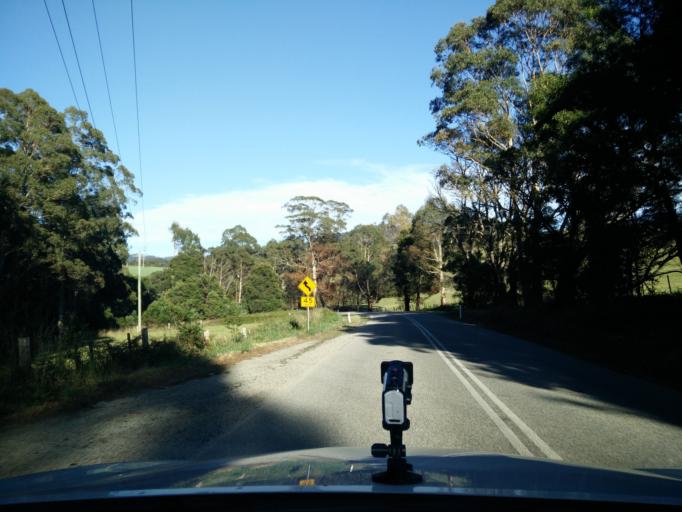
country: AU
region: Tasmania
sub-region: Break O'Day
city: St Helens
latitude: -41.2571
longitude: 148.0743
